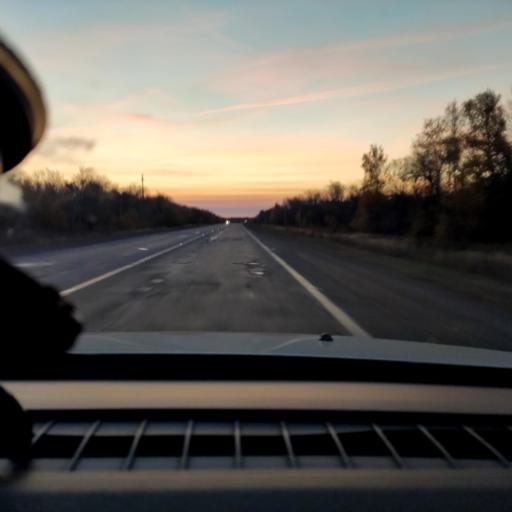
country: RU
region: Samara
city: Novokuybyshevsk
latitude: 52.9873
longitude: 49.8604
